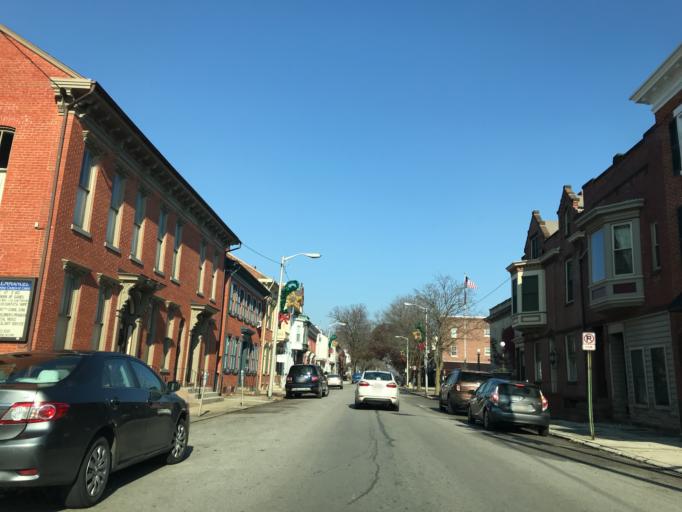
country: US
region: Pennsylvania
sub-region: York County
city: Hanover
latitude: 39.8017
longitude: -76.9821
